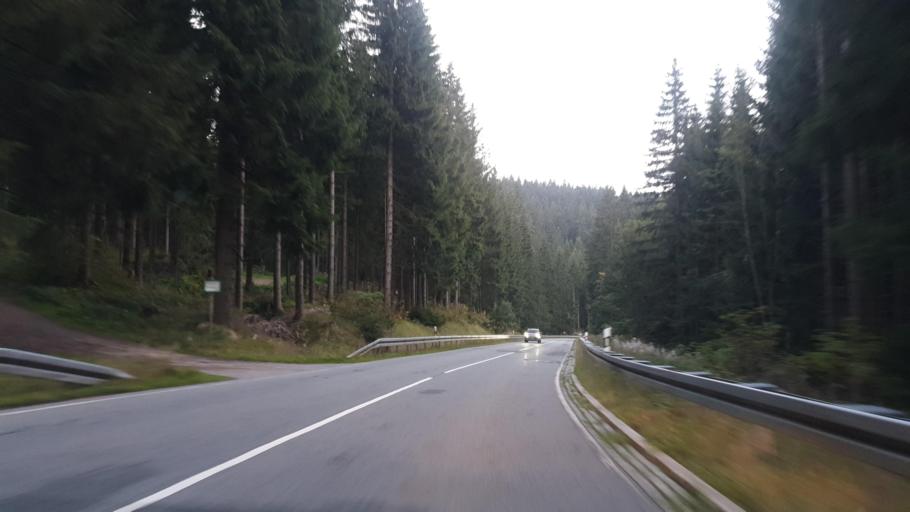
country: DE
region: Saxony
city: Johanngeorgenstadt
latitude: 50.4328
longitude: 12.6504
